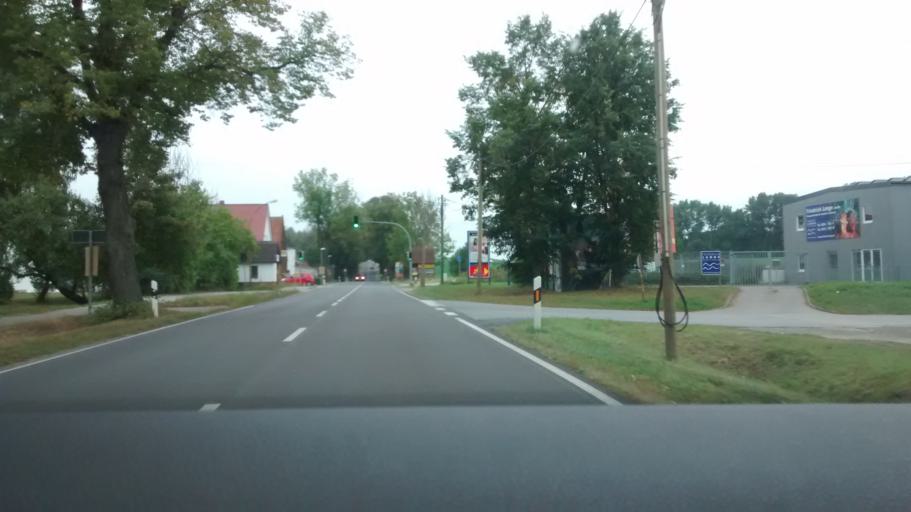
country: DE
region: Mecklenburg-Vorpommern
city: Mecklenburg
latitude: 53.8663
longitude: 11.4510
